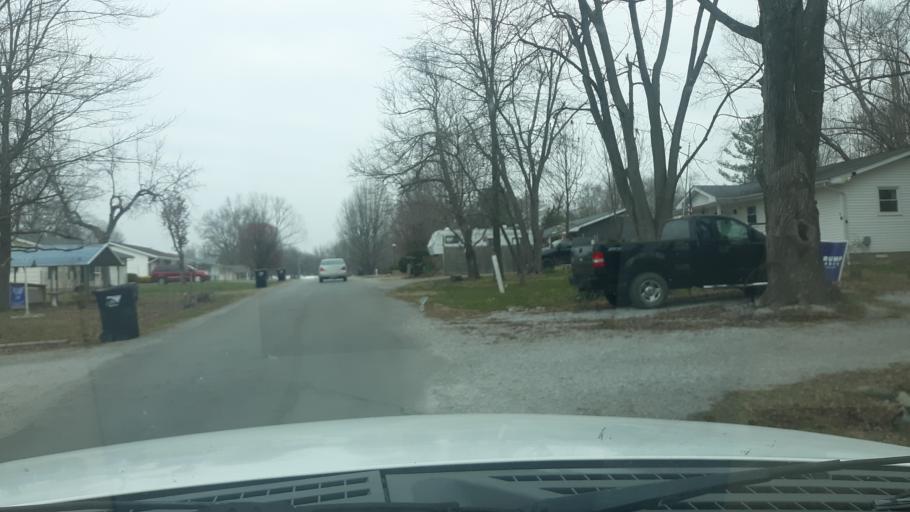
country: US
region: Illinois
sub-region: Saline County
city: Harrisburg
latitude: 37.8358
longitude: -88.6094
